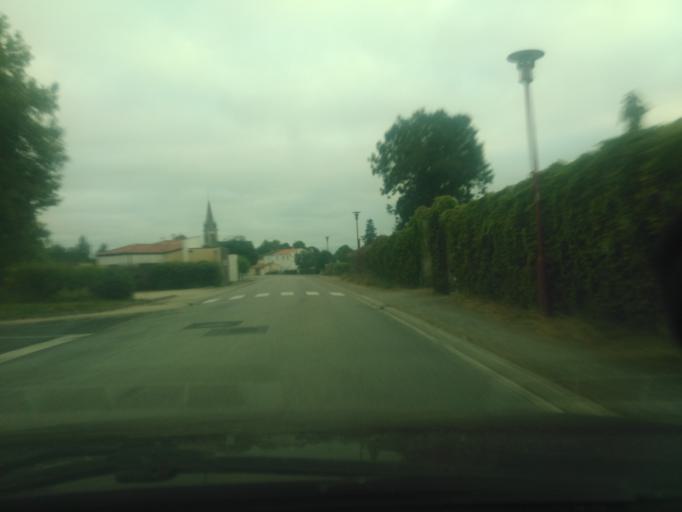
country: FR
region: Pays de la Loire
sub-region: Departement de la Vendee
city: Saint-Denis-la-Chevasse
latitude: 46.7922
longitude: -1.3182
